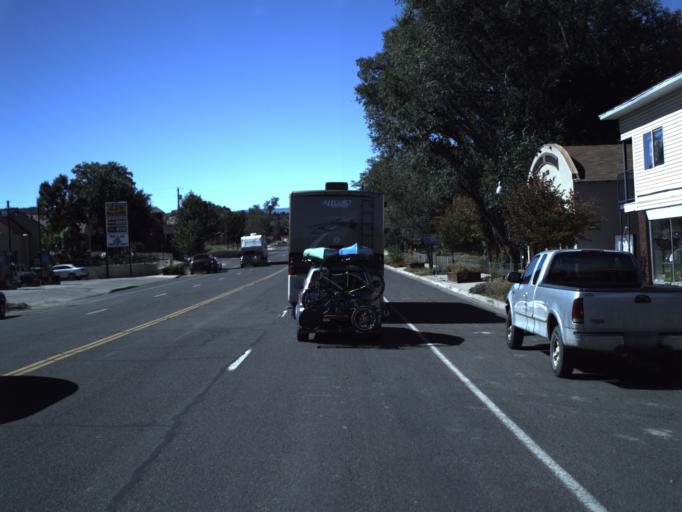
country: US
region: Utah
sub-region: Wayne County
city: Loa
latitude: 37.7704
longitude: -111.6007
